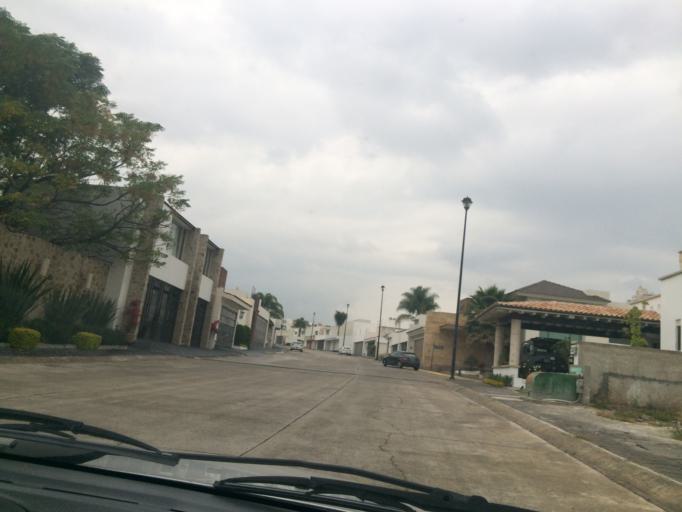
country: MX
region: Guanajuato
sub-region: Leon
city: La Ermita
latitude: 21.1709
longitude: -101.7074
